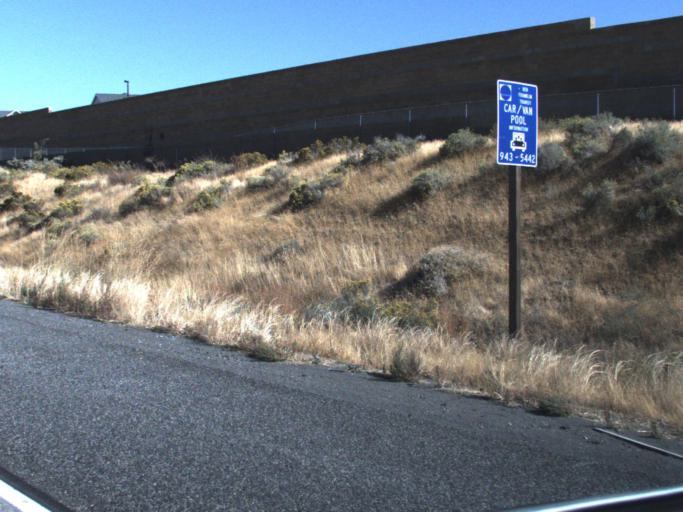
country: US
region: Washington
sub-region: Franklin County
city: West Pasco
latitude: 46.2720
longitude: -119.2292
